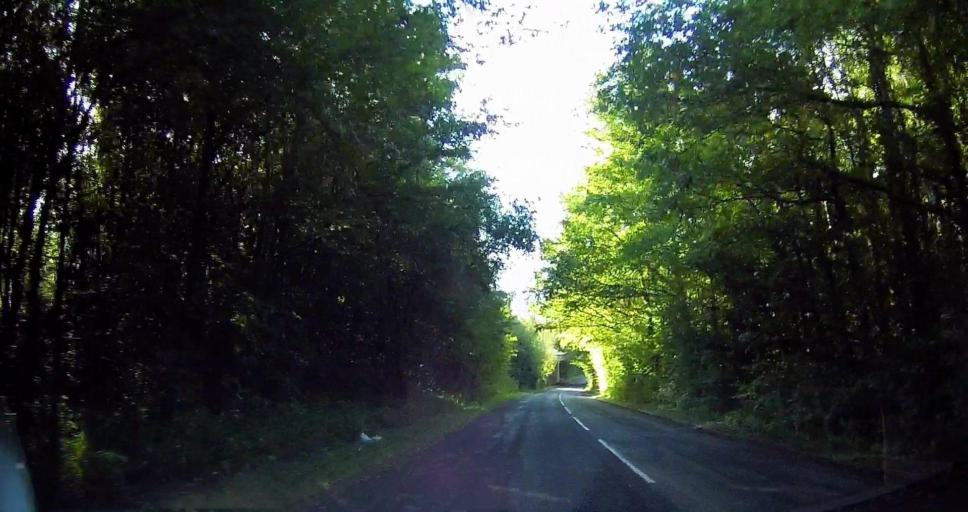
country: GB
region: England
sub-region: Kent
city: Borough Green
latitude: 51.3034
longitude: 0.2859
